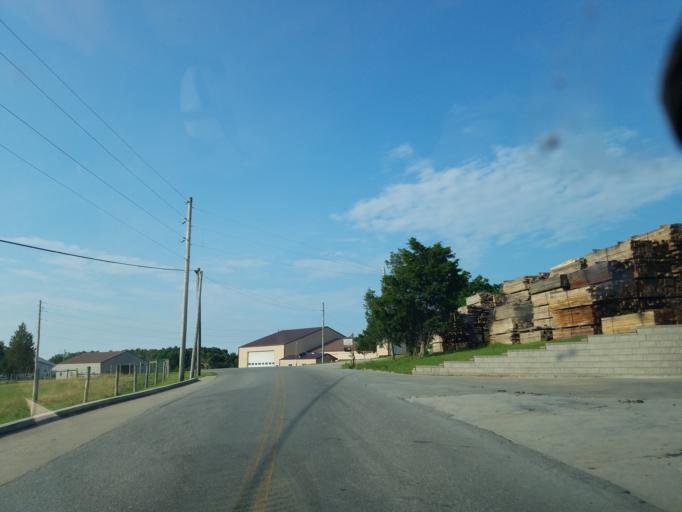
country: US
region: Ohio
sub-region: Adams County
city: West Union
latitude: 38.8971
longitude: -83.5195
